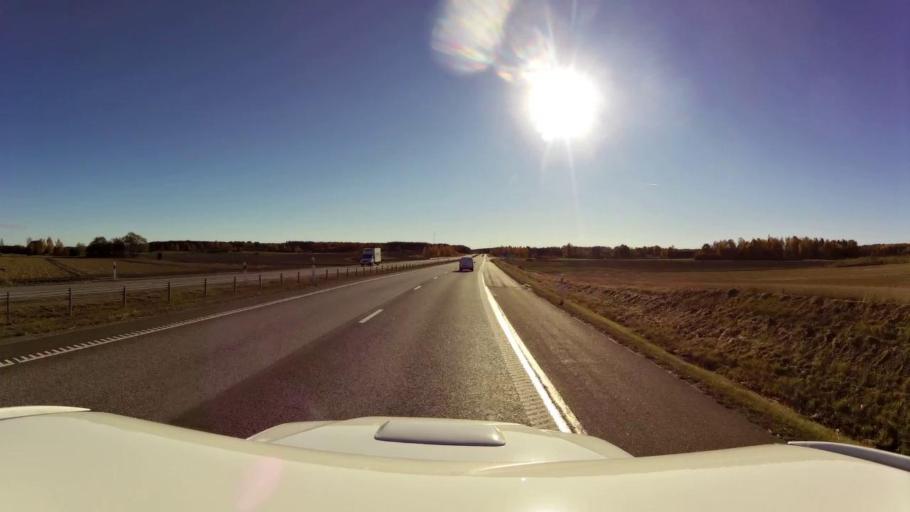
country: SE
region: OEstergoetland
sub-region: Linkopings Kommun
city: Malmslatt
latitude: 58.4306
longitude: 15.5334
